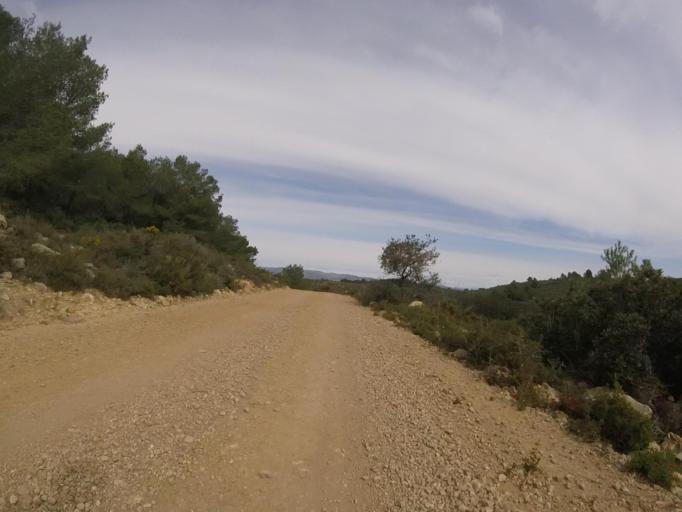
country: ES
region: Valencia
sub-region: Provincia de Castello
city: Cabanes
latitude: 40.1925
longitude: 0.0849
